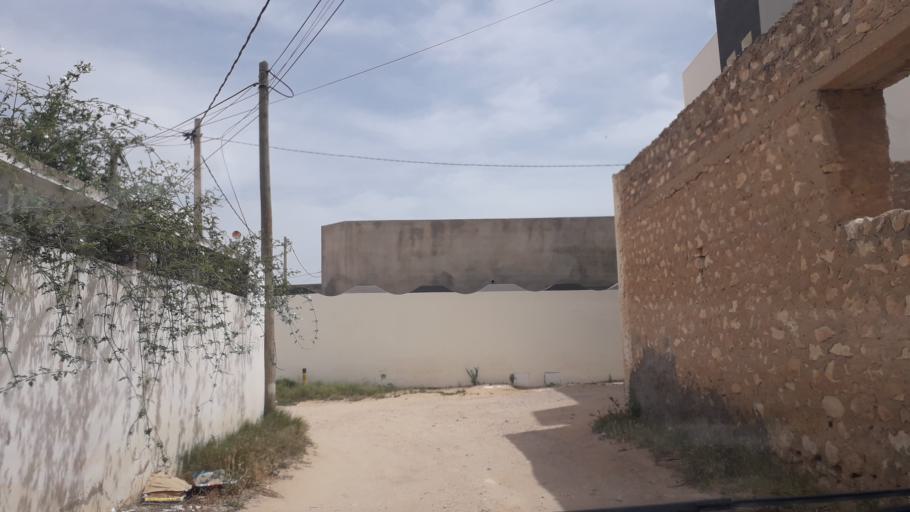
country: TN
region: Safaqis
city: Al Qarmadah
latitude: 34.8019
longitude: 10.7645
